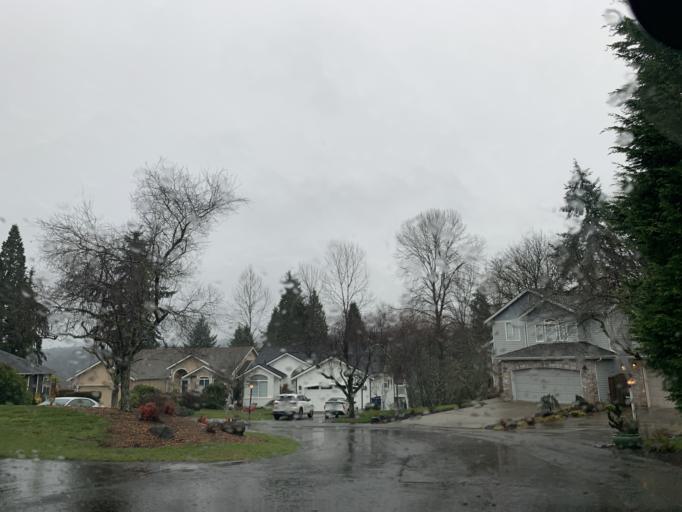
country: US
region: Washington
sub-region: King County
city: Woodinville
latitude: 47.7354
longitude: -122.1572
